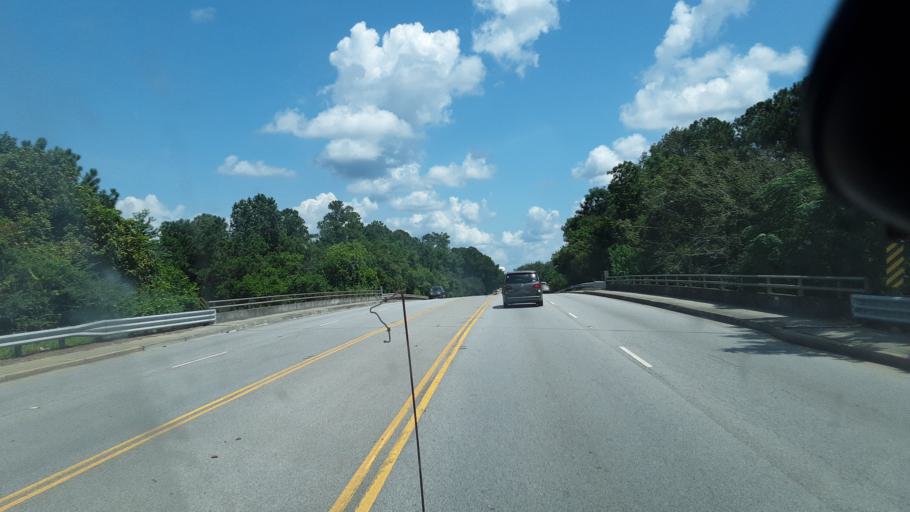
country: US
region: South Carolina
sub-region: Berkeley County
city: Moncks Corner
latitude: 33.1993
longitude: -80.0023
